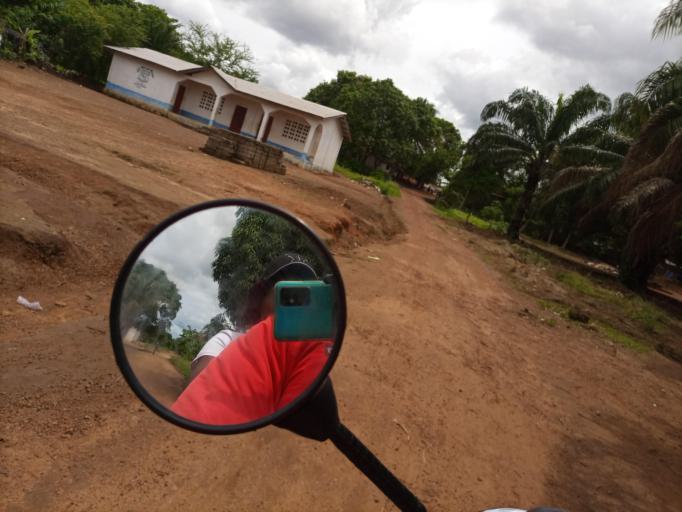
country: SL
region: Southern Province
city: Bo
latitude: 7.9690
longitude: -11.7163
